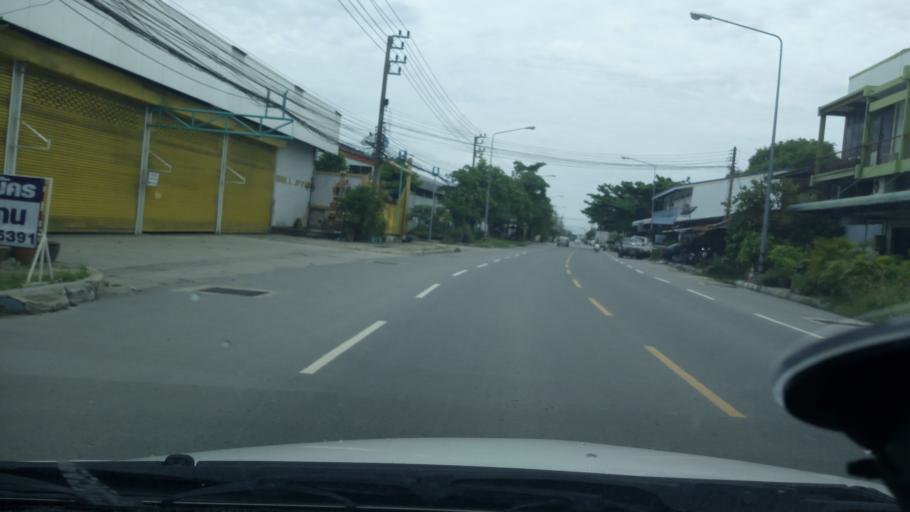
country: TH
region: Chon Buri
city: Chon Buri
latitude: 13.3350
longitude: 100.9966
